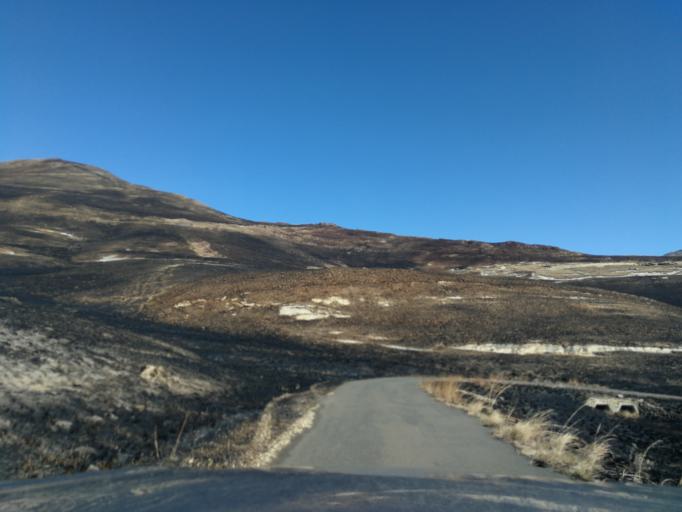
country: ZA
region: Orange Free State
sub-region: Thabo Mofutsanyana District Municipality
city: Phuthaditjhaba
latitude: -28.5209
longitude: 28.6215
